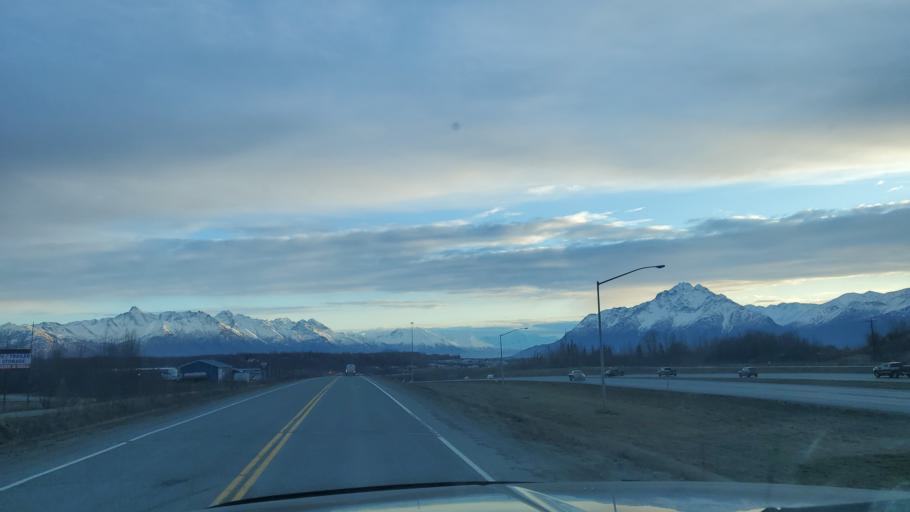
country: US
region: Alaska
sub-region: Matanuska-Susitna Borough
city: Lakes
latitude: 61.5693
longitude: -149.3363
